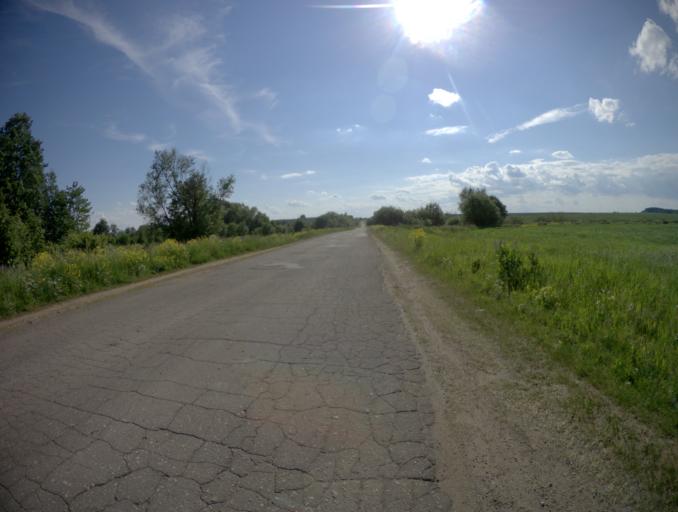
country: RU
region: Vladimir
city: Suzdal'
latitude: 56.3220
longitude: 40.4245
